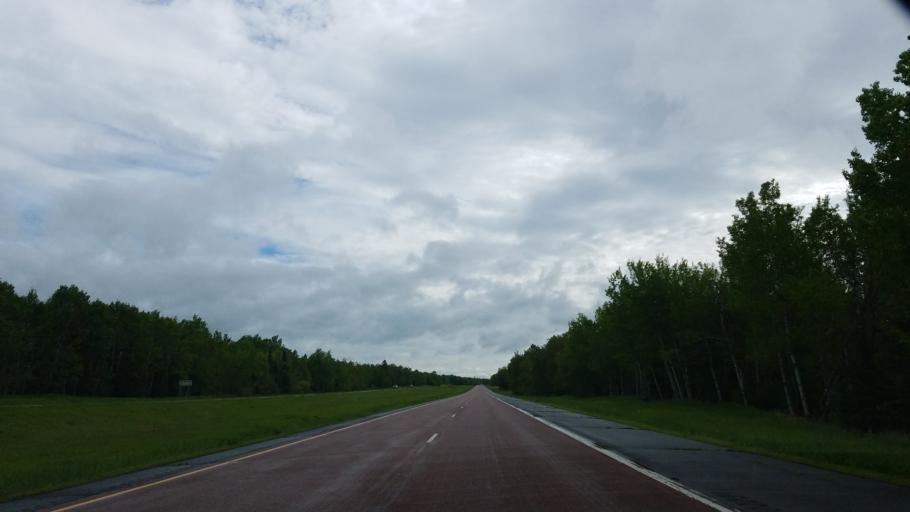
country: US
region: Minnesota
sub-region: Saint Louis County
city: Arnold
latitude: 46.8790
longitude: -91.9404
